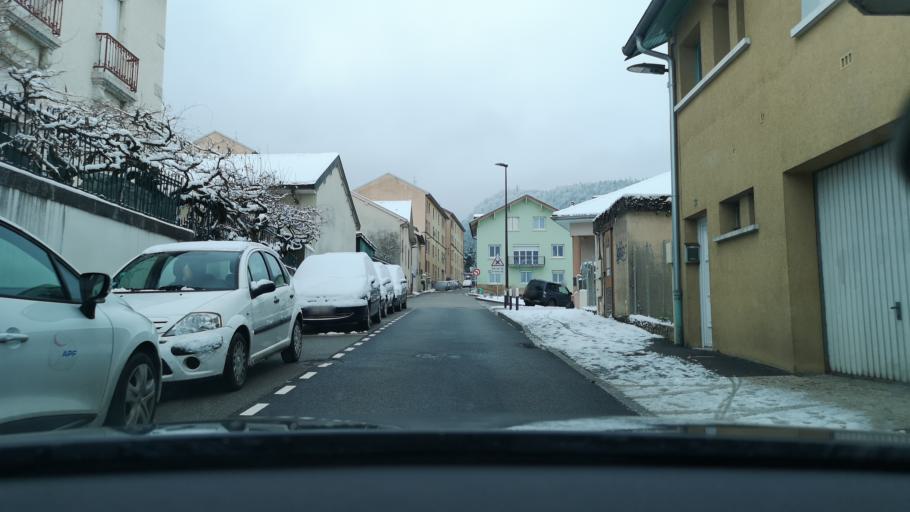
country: FR
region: Rhone-Alpes
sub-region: Departement de l'Ain
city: Oyonnax
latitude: 46.2583
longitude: 5.6620
